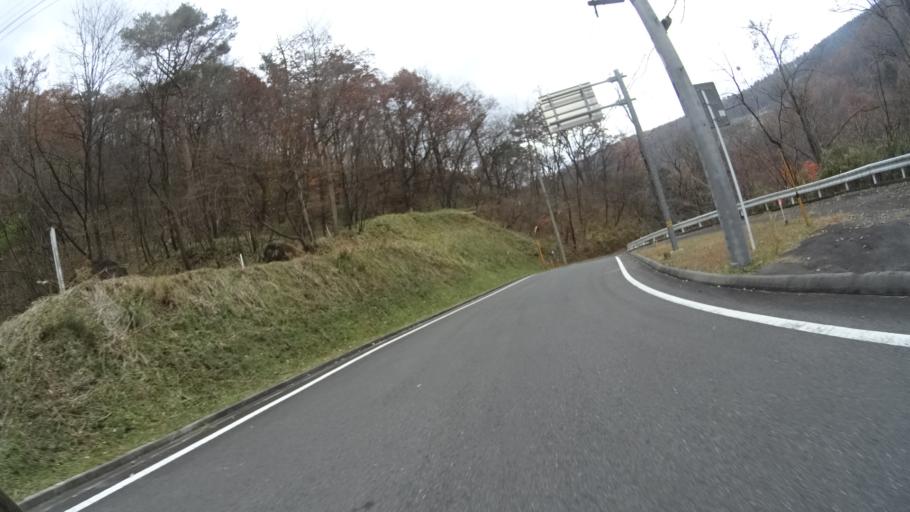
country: JP
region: Gunma
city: Omamacho-omama
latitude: 36.4948
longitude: 139.1847
